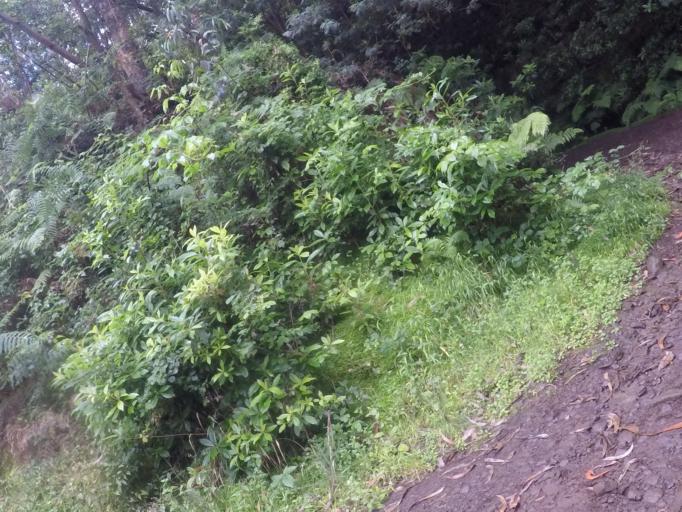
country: PT
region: Madeira
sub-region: Santana
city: Santana
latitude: 32.7762
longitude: -16.8790
